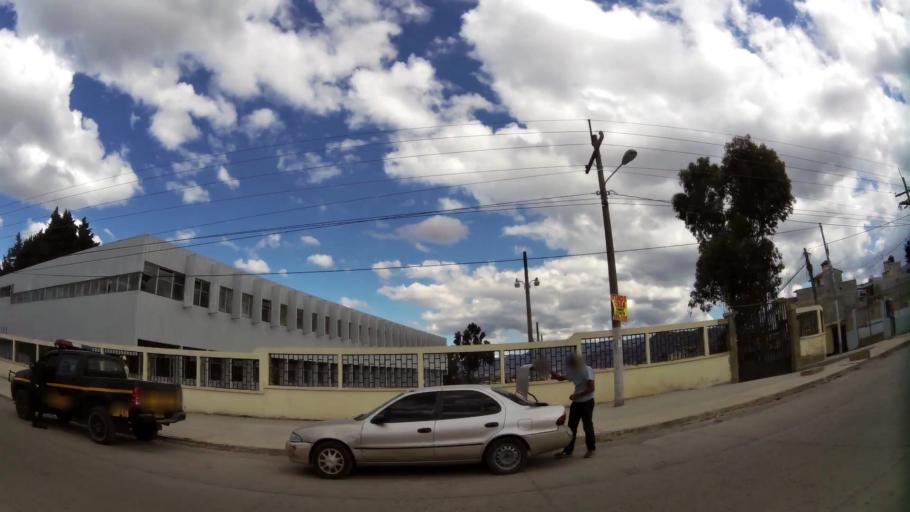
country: GT
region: Quetzaltenango
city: Quetzaltenango
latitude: 14.8445
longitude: -91.5365
